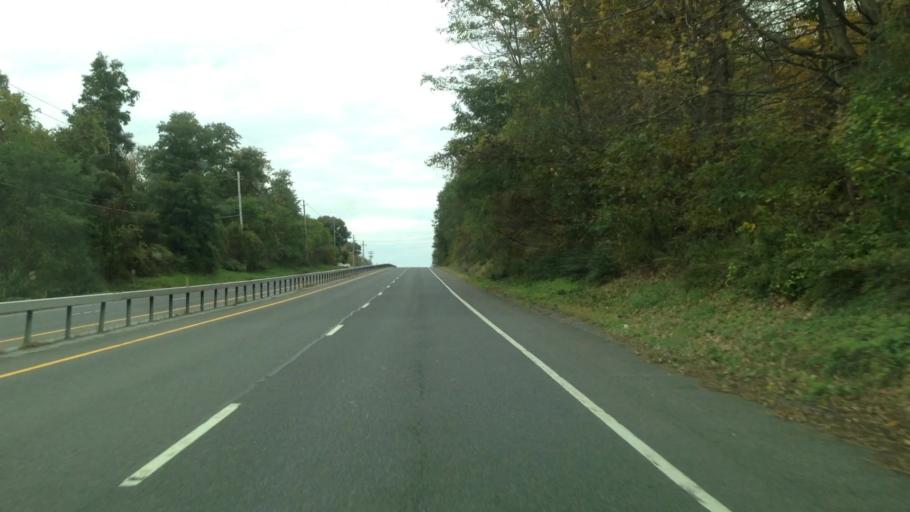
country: US
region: New York
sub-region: Dutchess County
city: Hyde Park
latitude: 41.7627
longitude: -73.9614
